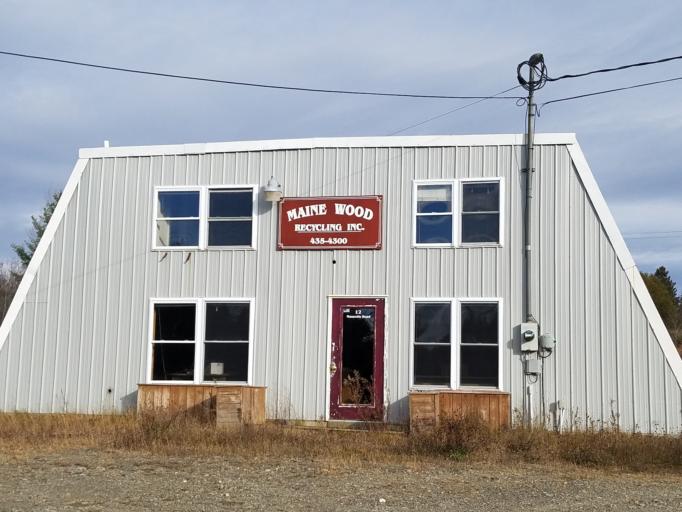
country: US
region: Maine
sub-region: Aroostook County
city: Presque Isle
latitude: 46.6257
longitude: -68.4016
